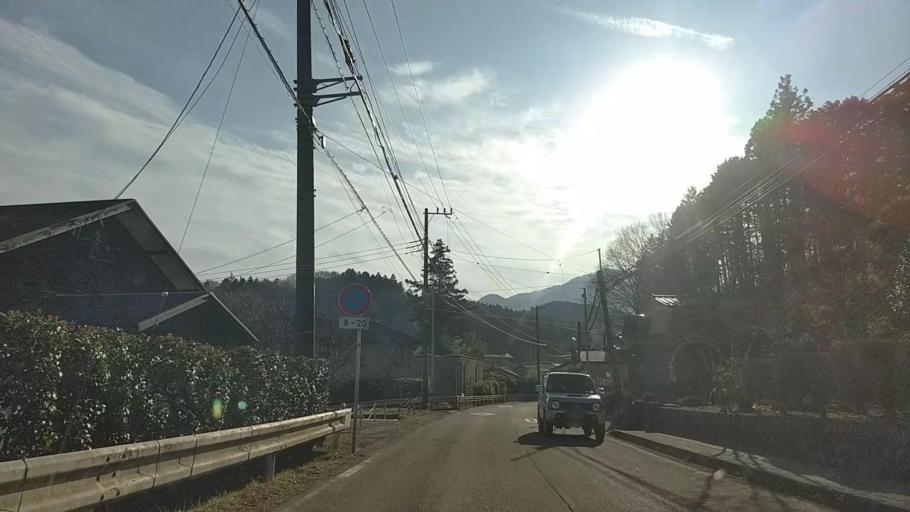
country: JP
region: Yamanashi
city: Uenohara
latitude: 35.5424
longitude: 139.2177
